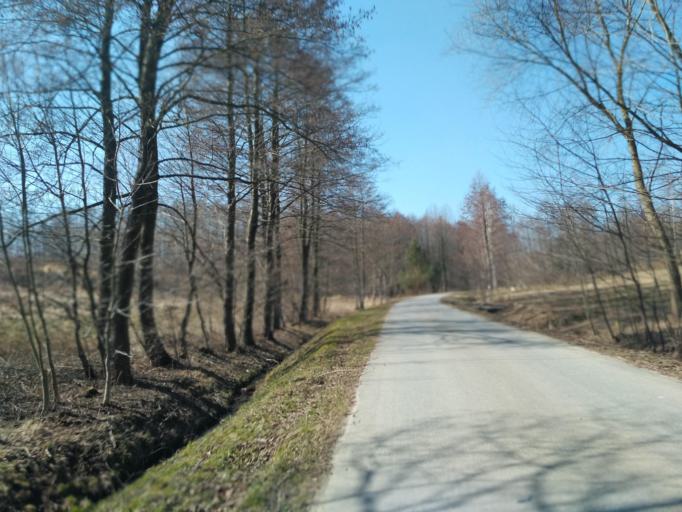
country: PL
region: Subcarpathian Voivodeship
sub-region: Powiat rzeszowski
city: Lutoryz
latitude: 49.9719
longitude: 21.8887
